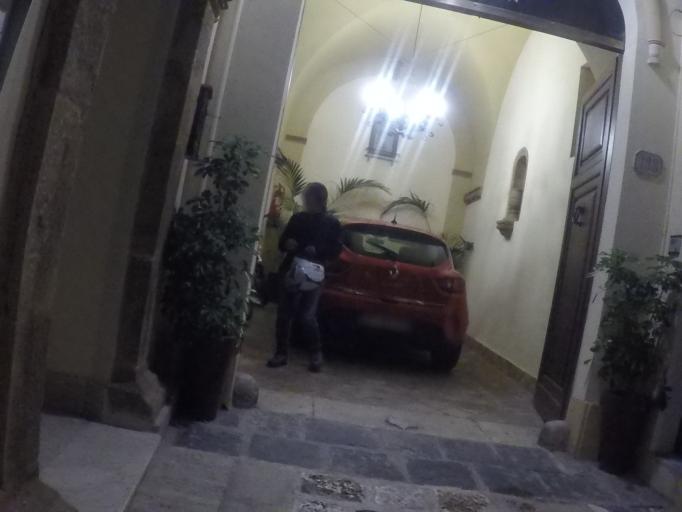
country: IT
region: Sicily
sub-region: Agrigento
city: Sciacca
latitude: 37.5089
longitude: 13.0795
